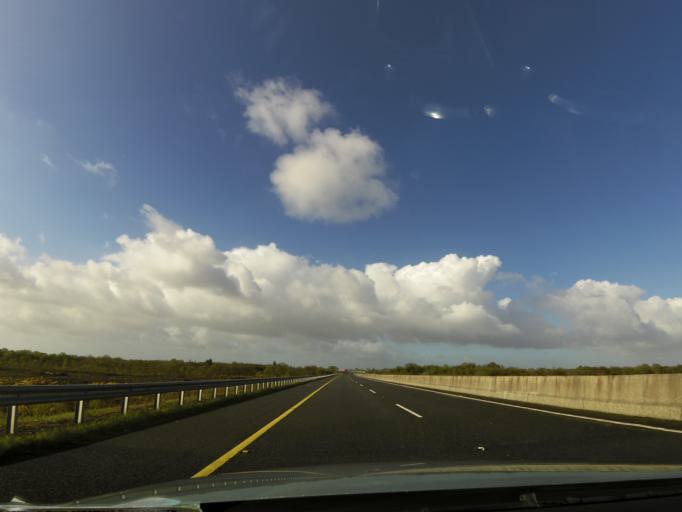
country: IE
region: Munster
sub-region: County Limerick
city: Castleconnell
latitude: 52.7157
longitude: -8.4744
